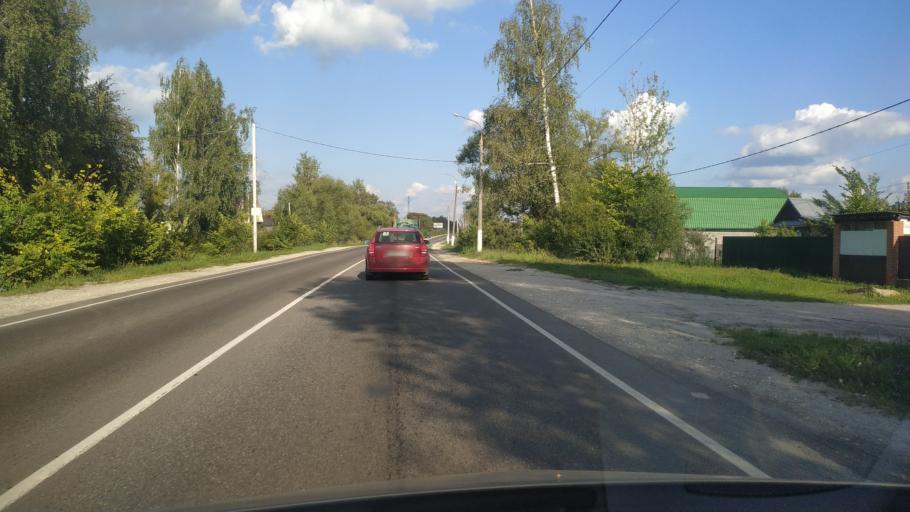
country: RU
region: Moskovskaya
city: Shaturtorf
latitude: 55.5796
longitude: 39.4674
